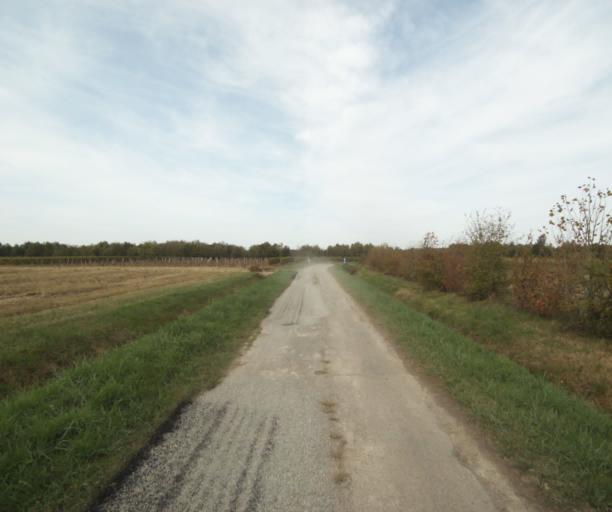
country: FR
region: Midi-Pyrenees
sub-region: Departement de la Haute-Garonne
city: Fronton
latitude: 43.8763
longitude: 1.3889
